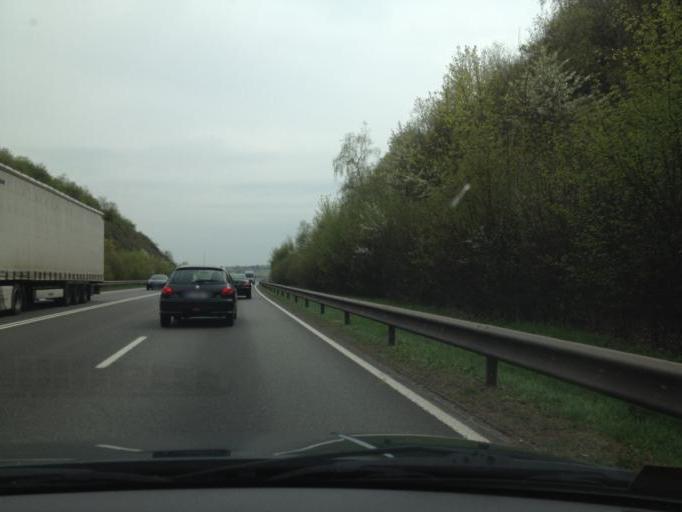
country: DE
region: Rheinland-Pfalz
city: Albersweiler
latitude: 49.2146
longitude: 8.0233
